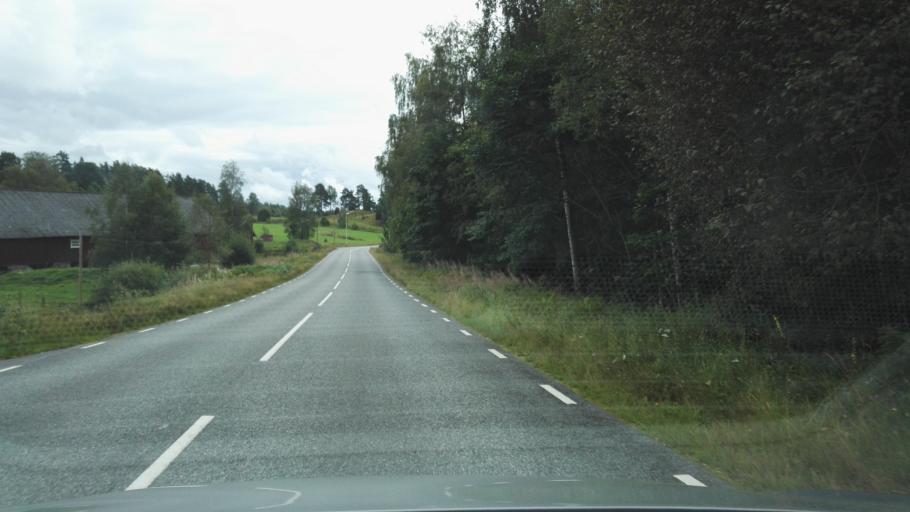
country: SE
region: Joenkoeping
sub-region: Vetlanda Kommun
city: Landsbro
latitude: 57.2265
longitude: 14.9476
